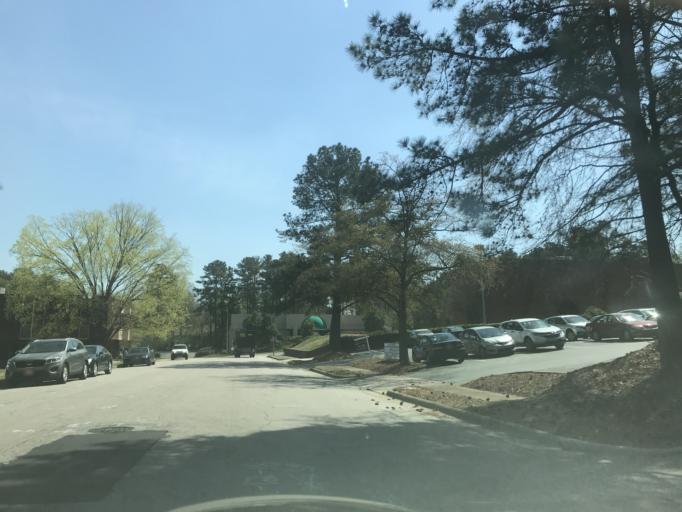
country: US
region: North Carolina
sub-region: Wake County
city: West Raleigh
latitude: 35.8290
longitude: -78.6336
